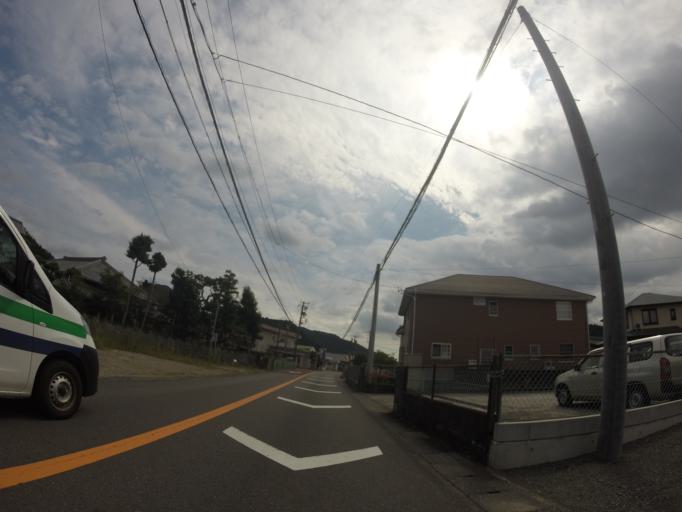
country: JP
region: Shizuoka
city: Shimada
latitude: 34.8560
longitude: 138.1808
